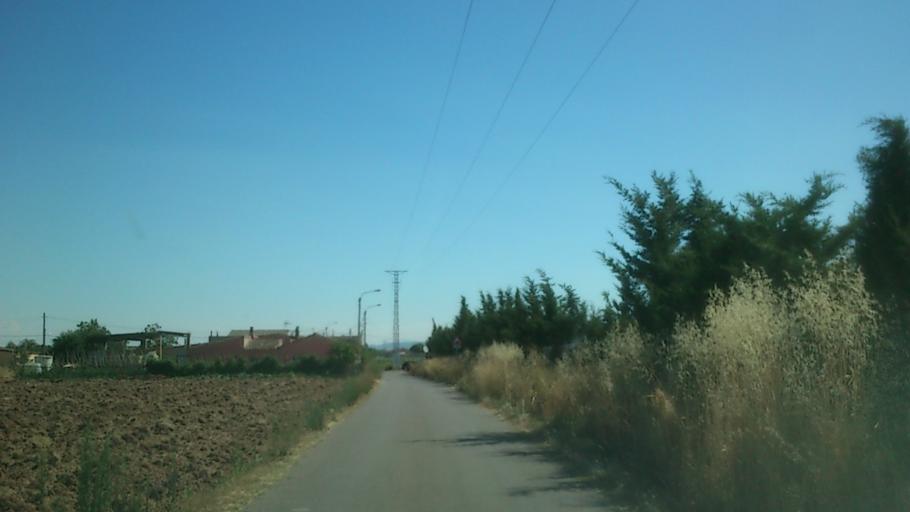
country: ES
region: Aragon
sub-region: Provincia de Zaragoza
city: Villanueva de Gallego
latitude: 41.7010
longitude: -0.8119
